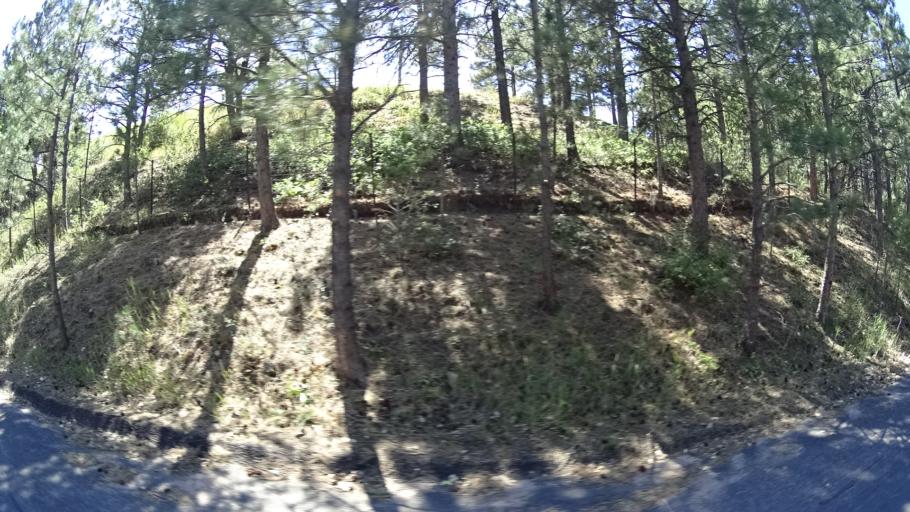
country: US
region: Colorado
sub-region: El Paso County
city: Colorado Springs
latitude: 38.7754
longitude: -104.8521
